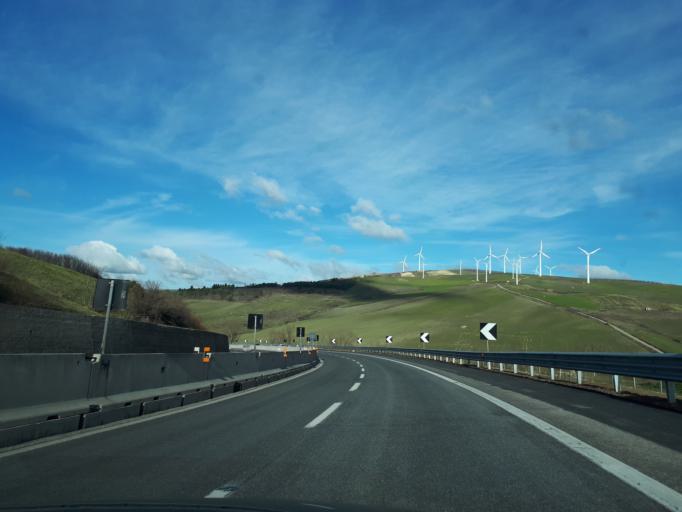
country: IT
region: Campania
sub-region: Provincia di Avellino
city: Vallesaccarda
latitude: 41.0752
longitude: 15.2628
